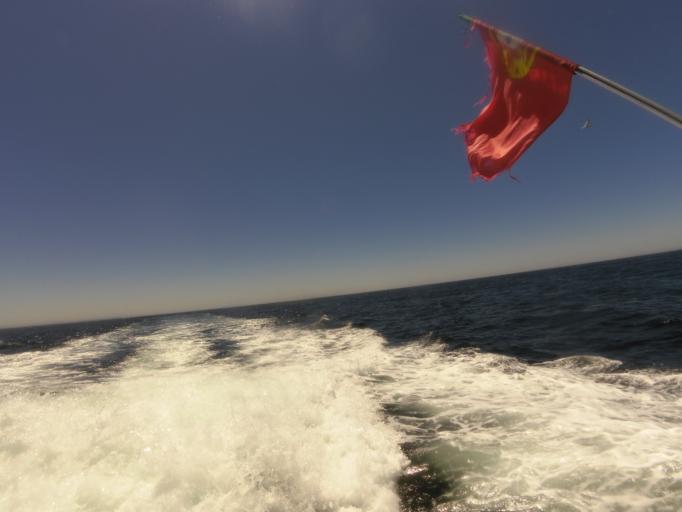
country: PT
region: Leiria
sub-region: Peniche
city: Peniche
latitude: 39.4098
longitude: -9.5012
